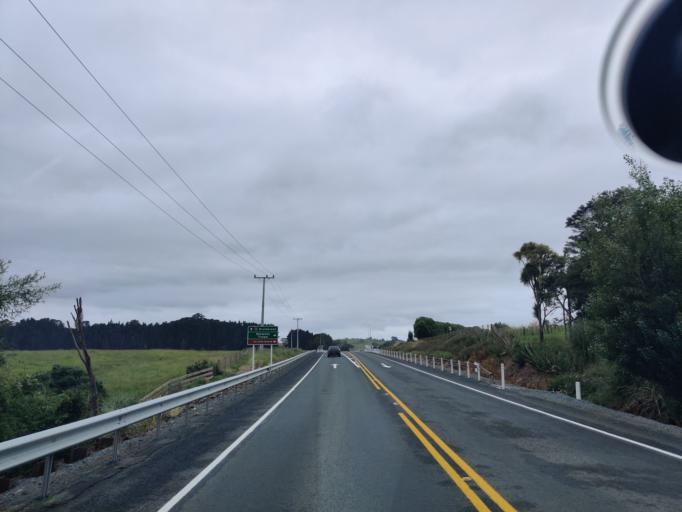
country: NZ
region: Northland
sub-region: Whangarei
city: Ruakaka
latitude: -36.1240
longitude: 174.1771
